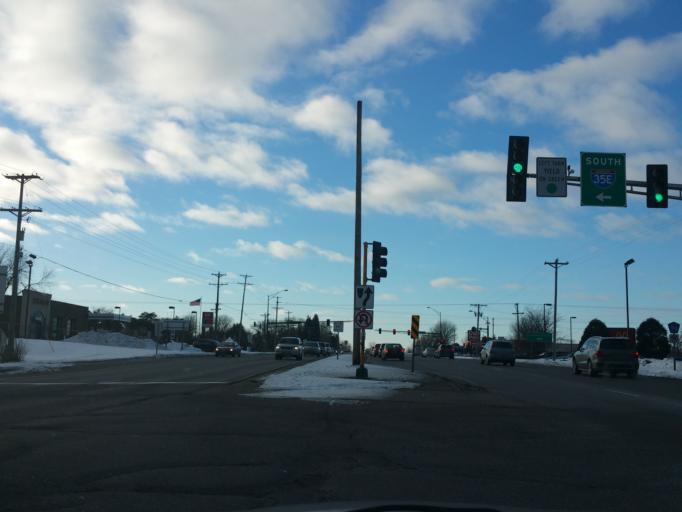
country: US
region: Minnesota
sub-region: Ramsey County
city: Vadnais Heights
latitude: 45.0793
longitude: -93.0541
